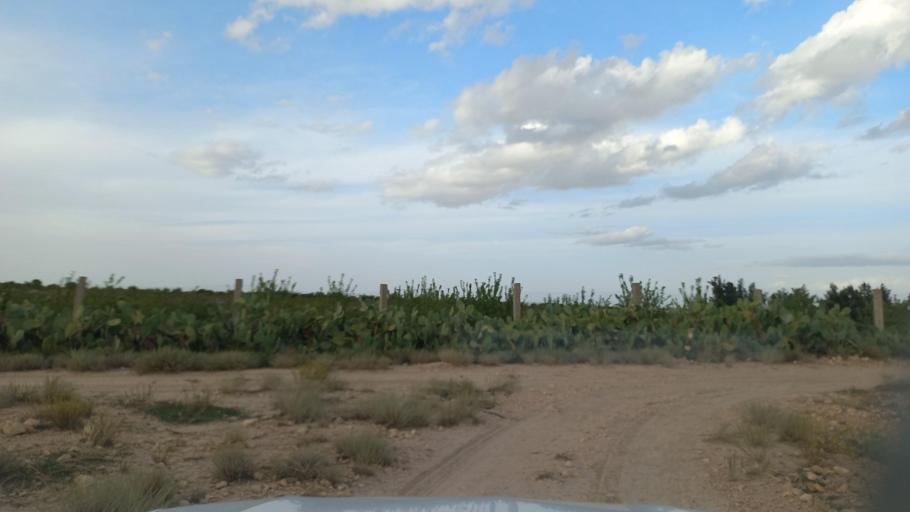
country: TN
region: Al Qasrayn
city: Sbiba
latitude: 35.4408
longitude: 9.0915
